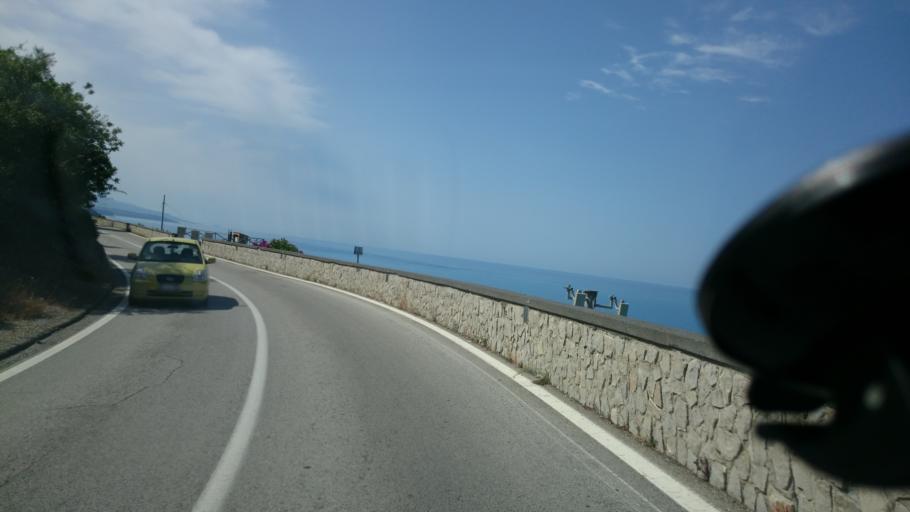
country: IT
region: Basilicate
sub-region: Provincia di Potenza
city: Maratea
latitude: 39.9865
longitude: 15.7130
